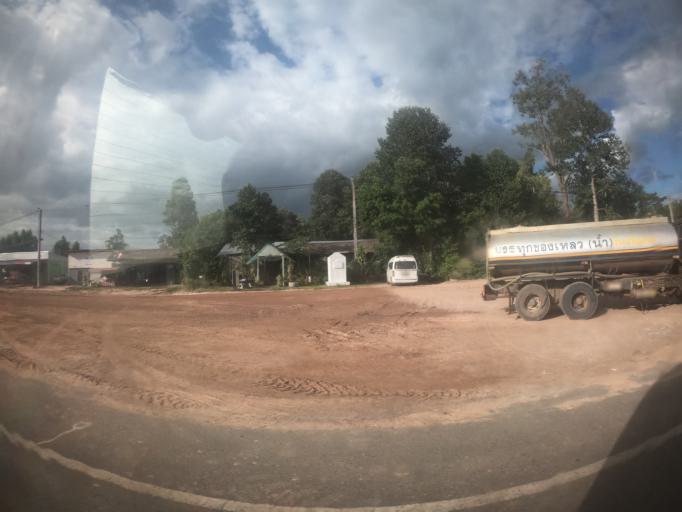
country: TH
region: Surin
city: Kap Choeng
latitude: 14.4792
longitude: 103.5864
